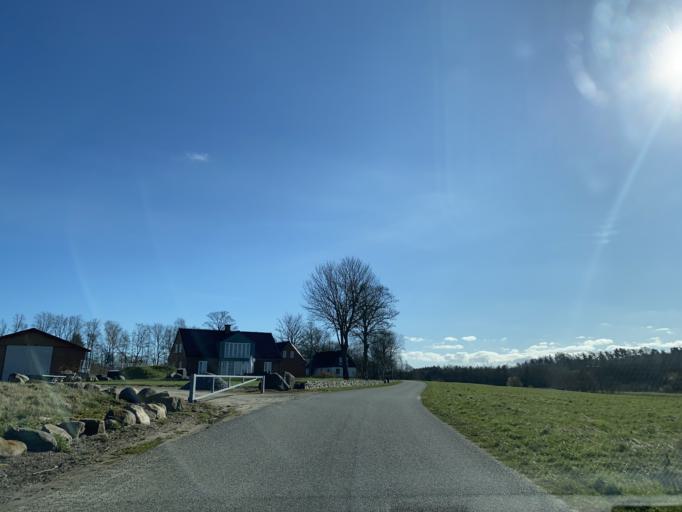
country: DK
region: Central Jutland
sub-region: Arhus Kommune
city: Framlev
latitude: 56.1811
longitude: 10.0311
